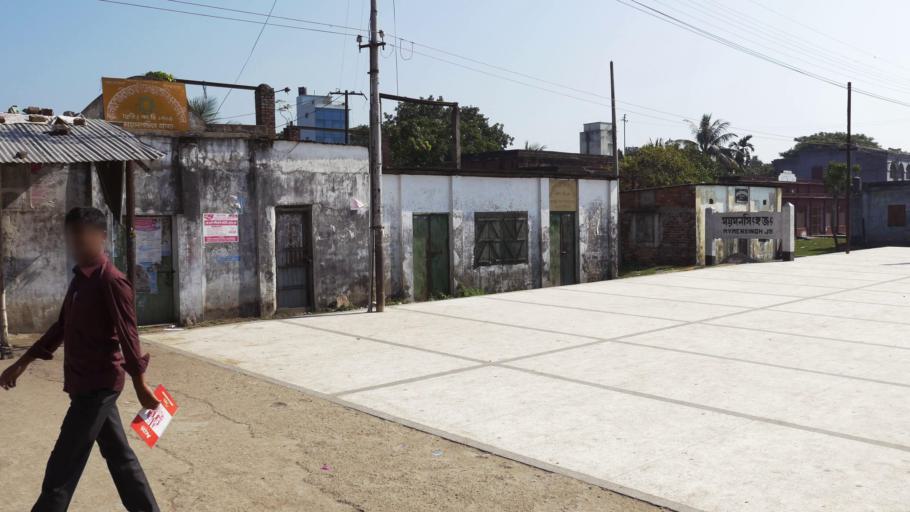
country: BD
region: Dhaka
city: Mymensingh
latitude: 24.6456
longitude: 90.4541
